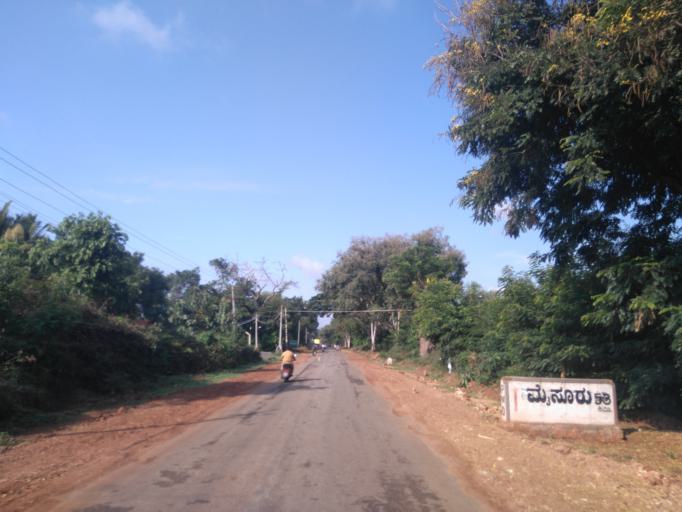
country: IN
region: Karnataka
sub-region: Mysore
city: Tirumakudal Narsipur
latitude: 12.2607
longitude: 77.0155
